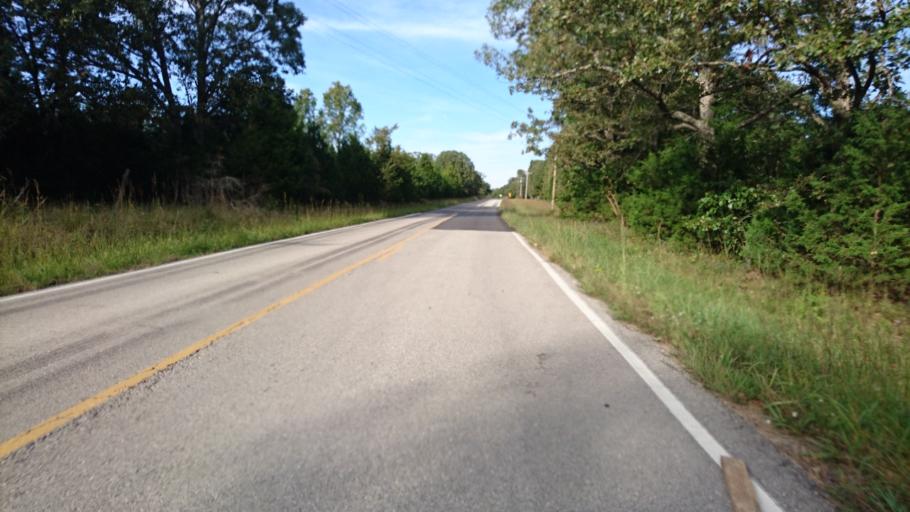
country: US
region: Missouri
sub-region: Crawford County
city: Cuba
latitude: 38.1083
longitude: -91.3608
